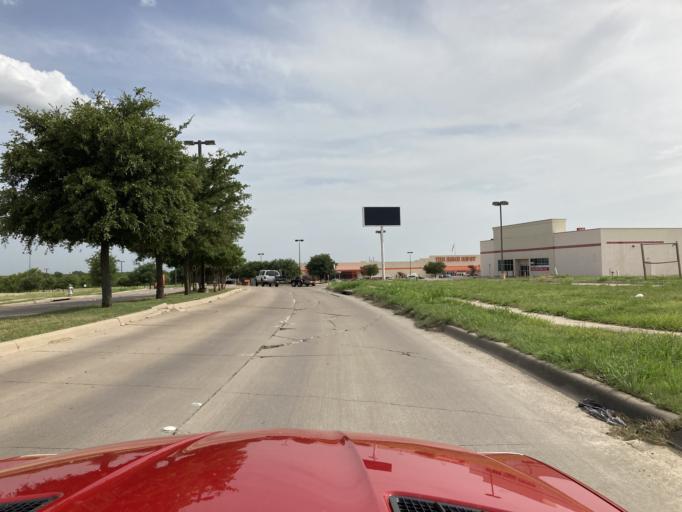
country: US
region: Texas
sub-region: Navarro County
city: Corsicana
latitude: 32.0679
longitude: -96.4484
